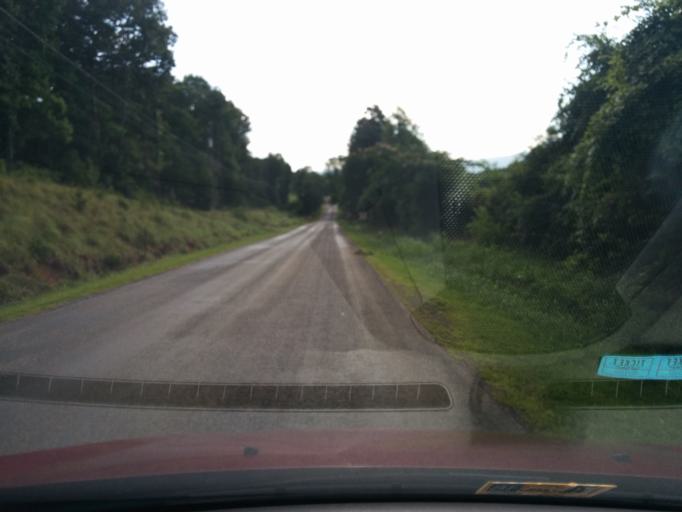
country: US
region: Virginia
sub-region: Rockbridge County
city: Glasgow
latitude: 37.6509
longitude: -79.5181
